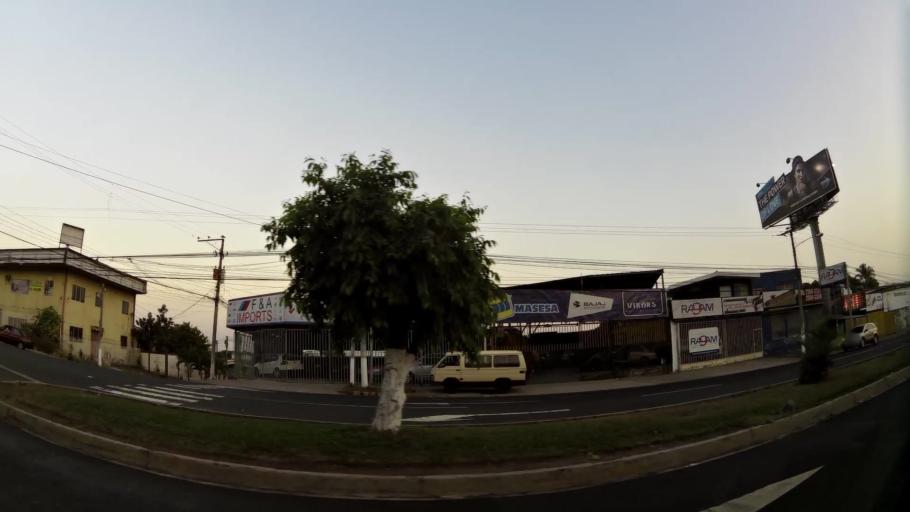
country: SV
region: San Salvador
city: Mejicanos
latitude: 13.7108
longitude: -89.2256
